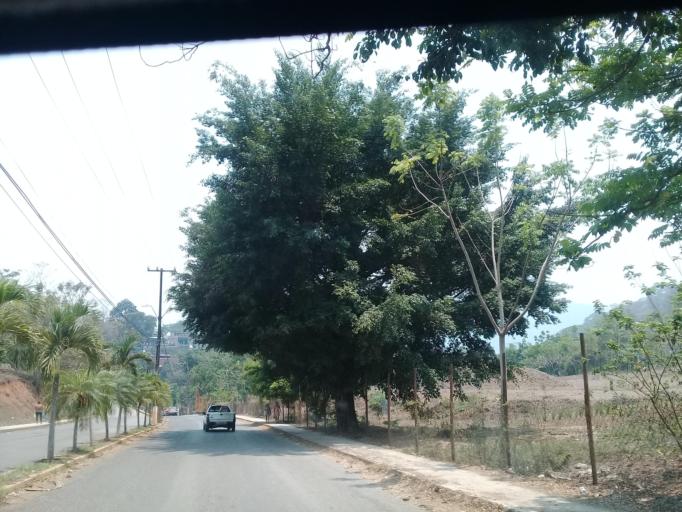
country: MX
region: Veracruz
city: Tezonapa
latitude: 18.6082
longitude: -96.6896
